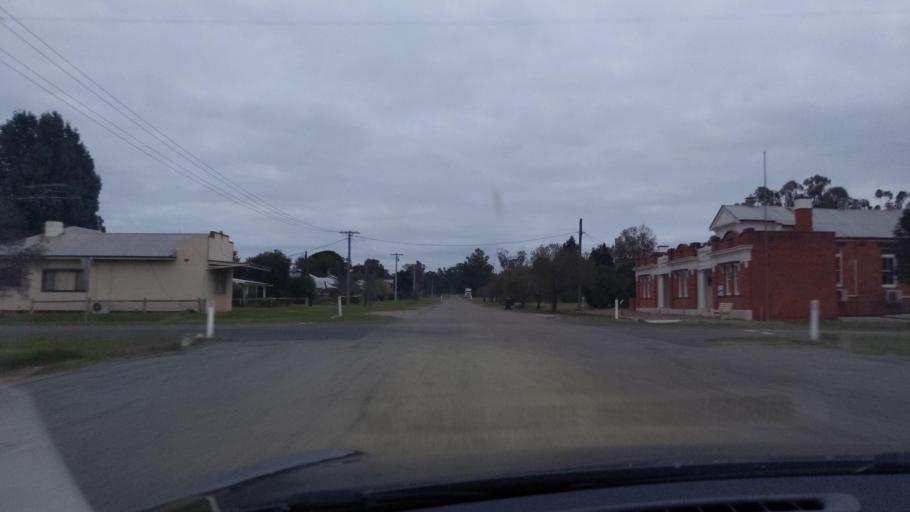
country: AU
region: New South Wales
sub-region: Narrandera
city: Narrandera
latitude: -34.7377
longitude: 146.7830
